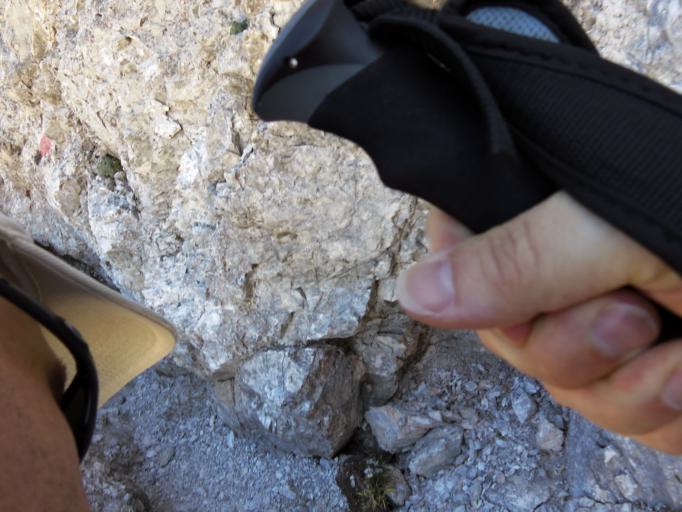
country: AT
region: Tyrol
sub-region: Politischer Bezirk Innsbruck Land
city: Neustift im Stubaital
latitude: 47.1392
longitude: 11.2752
